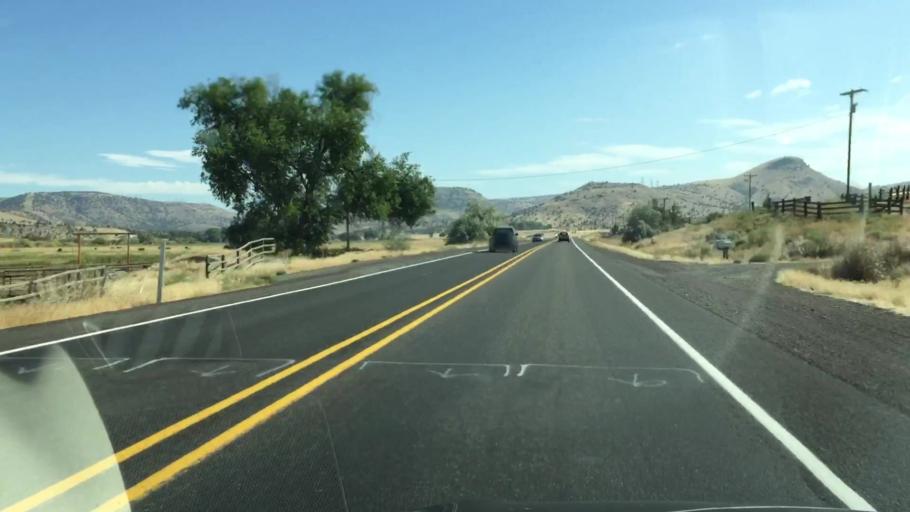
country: US
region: Oregon
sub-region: Jefferson County
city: Madras
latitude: 44.7974
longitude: -120.9483
